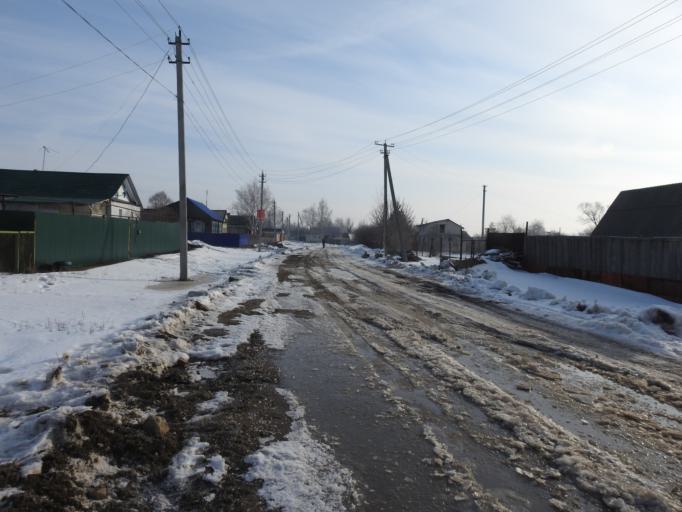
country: RU
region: Saratov
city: Krasnyy Oktyabr'
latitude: 51.4954
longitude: 45.7373
